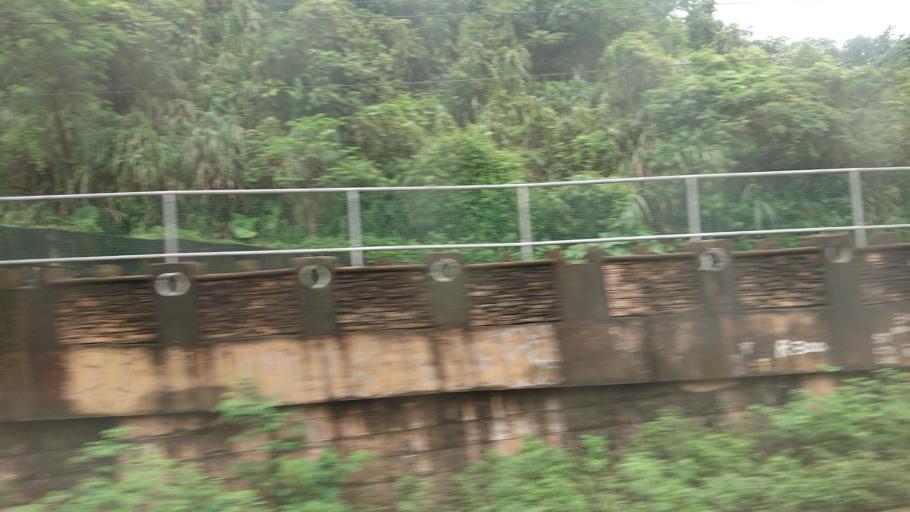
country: TW
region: Taiwan
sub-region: Keelung
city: Keelung
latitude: 25.0837
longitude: 121.7047
